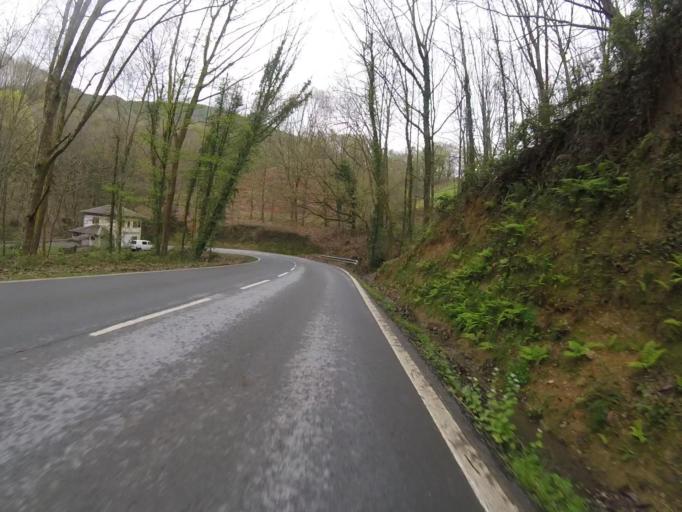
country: ES
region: Navarre
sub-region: Provincia de Navarra
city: Etxalar
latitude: 43.2810
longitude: -1.6313
